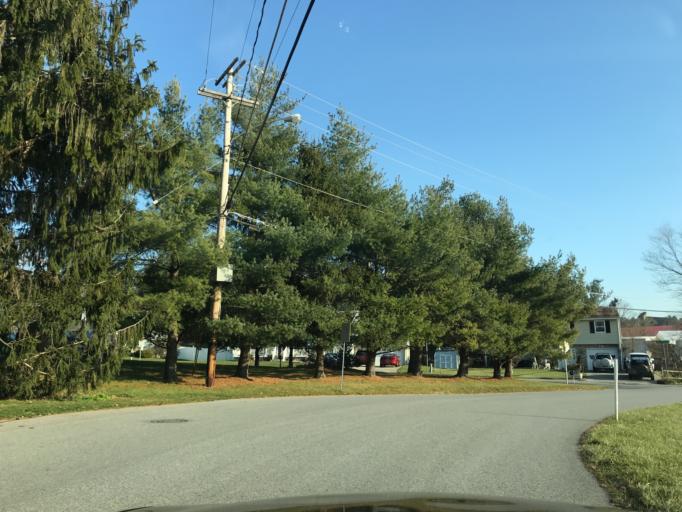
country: US
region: Pennsylvania
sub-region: York County
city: New Freedom
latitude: 39.7455
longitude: -76.6971
